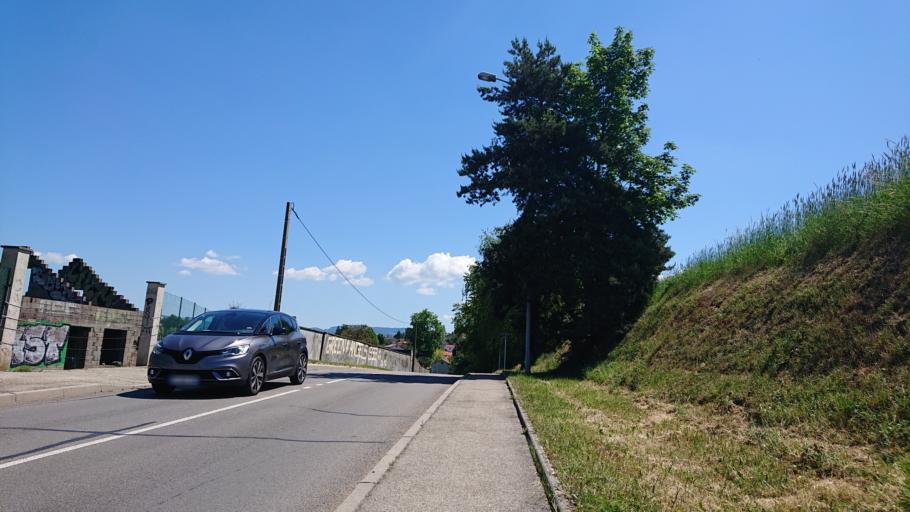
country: FR
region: Rhone-Alpes
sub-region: Departement de la Loire
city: Villars
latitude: 45.4559
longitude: 4.3552
